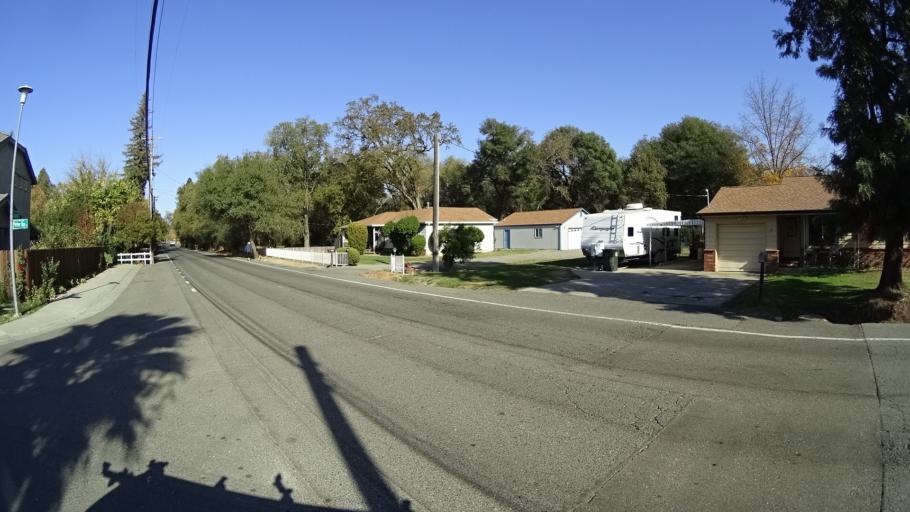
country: US
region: California
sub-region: Sacramento County
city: Citrus Heights
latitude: 38.6870
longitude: -121.2833
